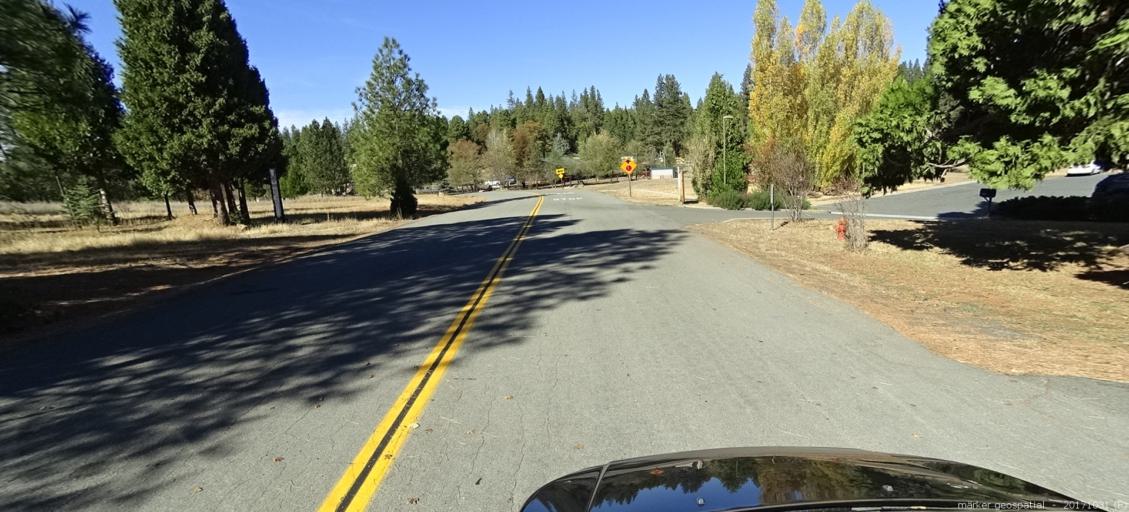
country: US
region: California
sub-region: Shasta County
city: Shingletown
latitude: 40.4913
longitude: -121.8855
